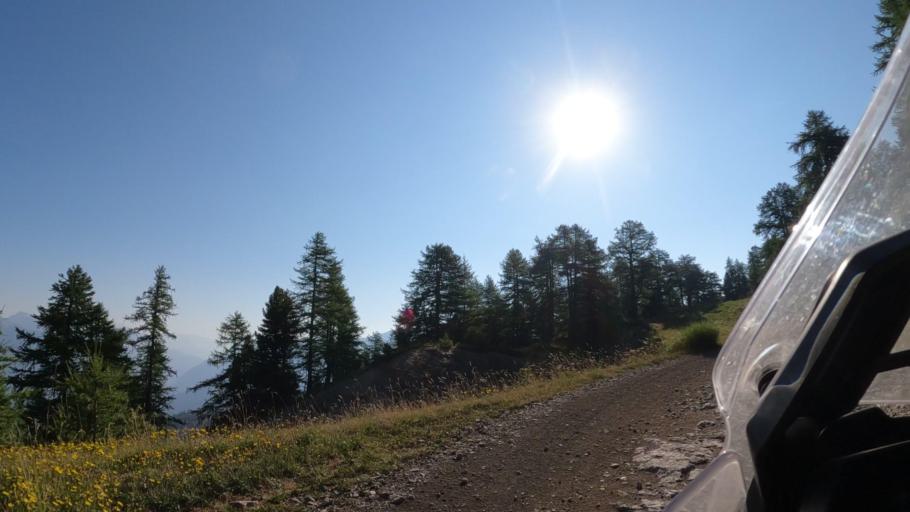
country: FR
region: Provence-Alpes-Cote d'Azur
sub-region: Departement des Hautes-Alpes
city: Guillestre
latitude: 44.6085
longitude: 6.6260
